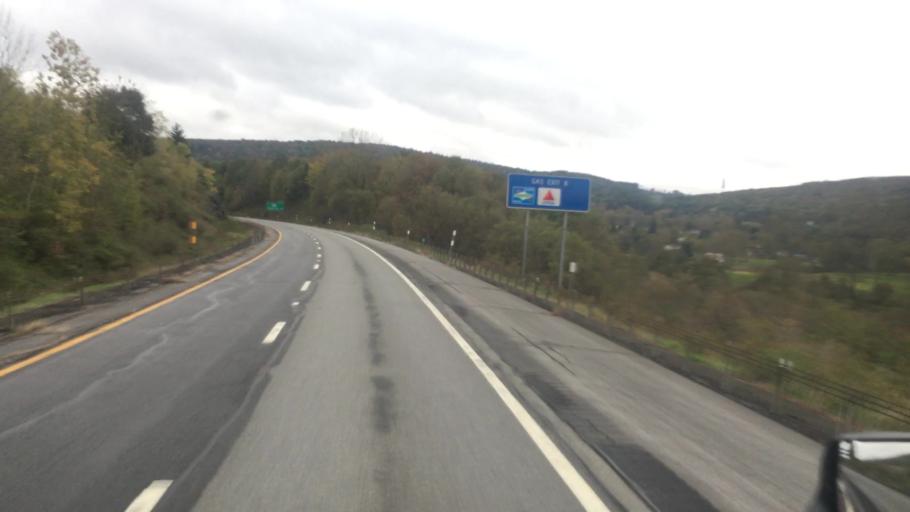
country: US
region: New York
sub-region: Chenango County
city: Bainbridge
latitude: 42.2948
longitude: -75.4617
